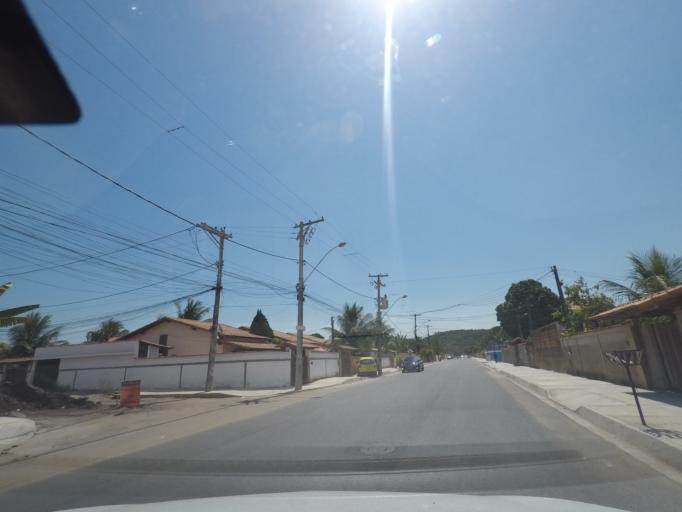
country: BR
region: Rio de Janeiro
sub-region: Marica
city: Marica
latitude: -22.9567
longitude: -42.9630
